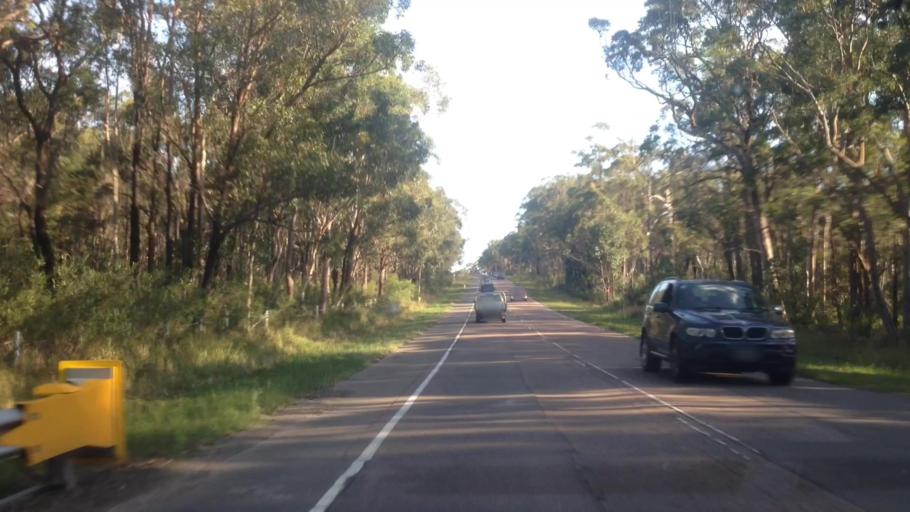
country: AU
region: New South Wales
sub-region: Lake Macquarie Shire
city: Dora Creek
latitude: -33.1395
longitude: 151.4776
